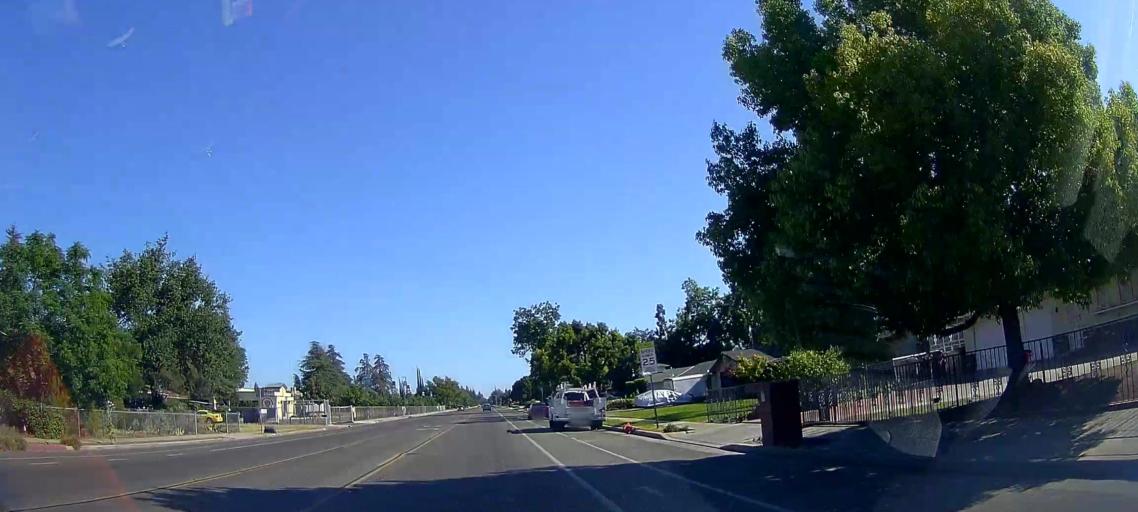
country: US
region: California
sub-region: Fresno County
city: Fresno
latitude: 36.8190
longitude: -119.7994
